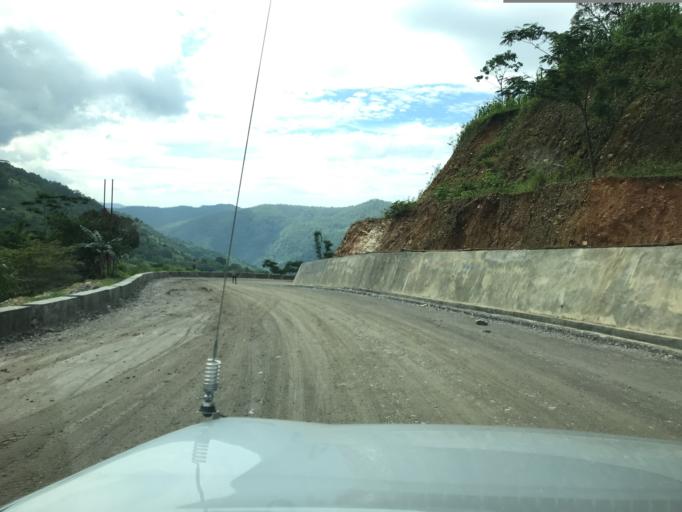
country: TL
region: Aileu
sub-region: Aileu Villa
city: Aileu
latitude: -8.6537
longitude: 125.5276
